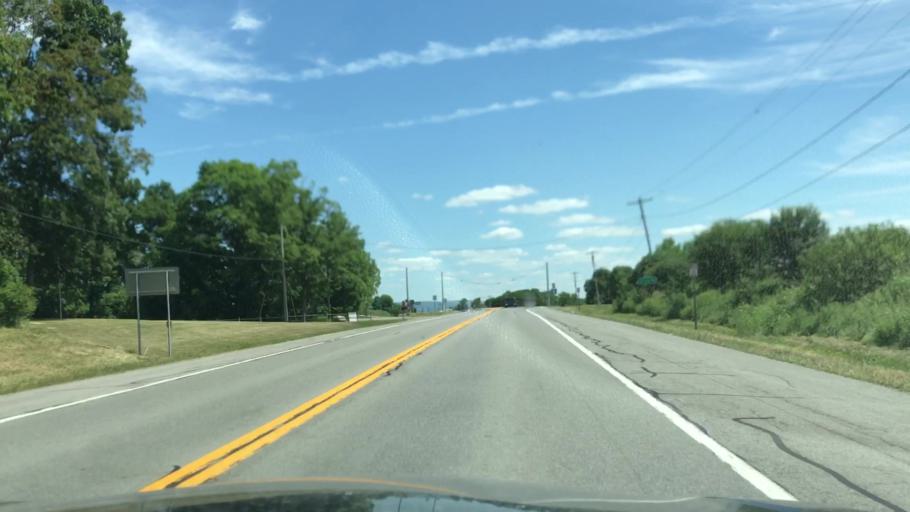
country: US
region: New York
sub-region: Livingston County
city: Mount Morris
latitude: 42.6736
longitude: -77.8144
